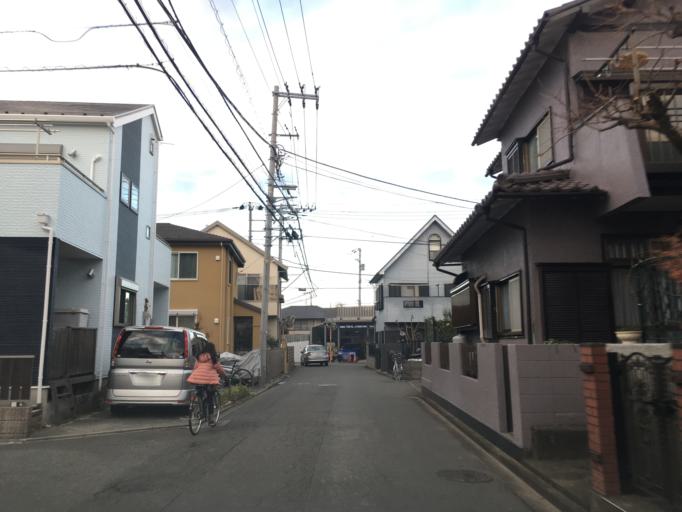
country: JP
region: Tokyo
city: Hachioji
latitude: 35.5934
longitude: 139.3690
